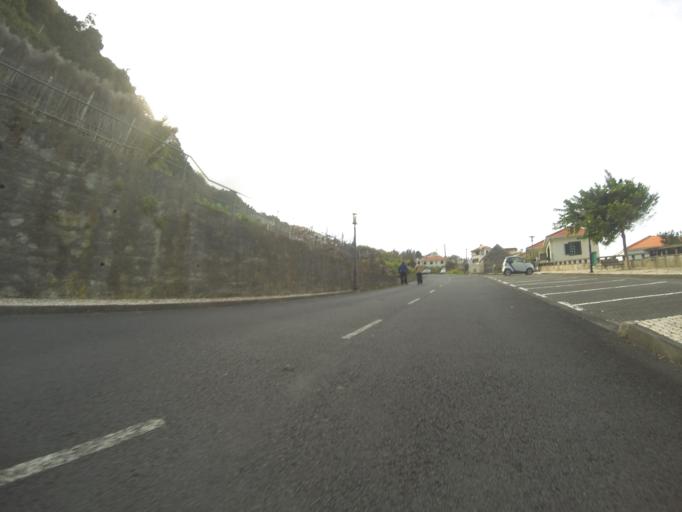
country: PT
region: Madeira
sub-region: Sao Vicente
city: Sao Vicente
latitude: 32.8217
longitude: -17.1042
